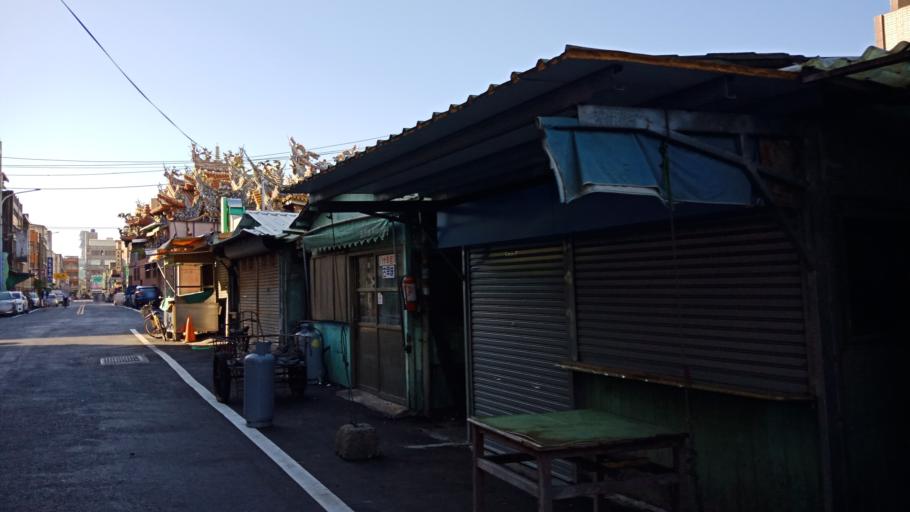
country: TW
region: Taiwan
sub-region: Miaoli
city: Miaoli
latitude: 24.4889
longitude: 120.6810
